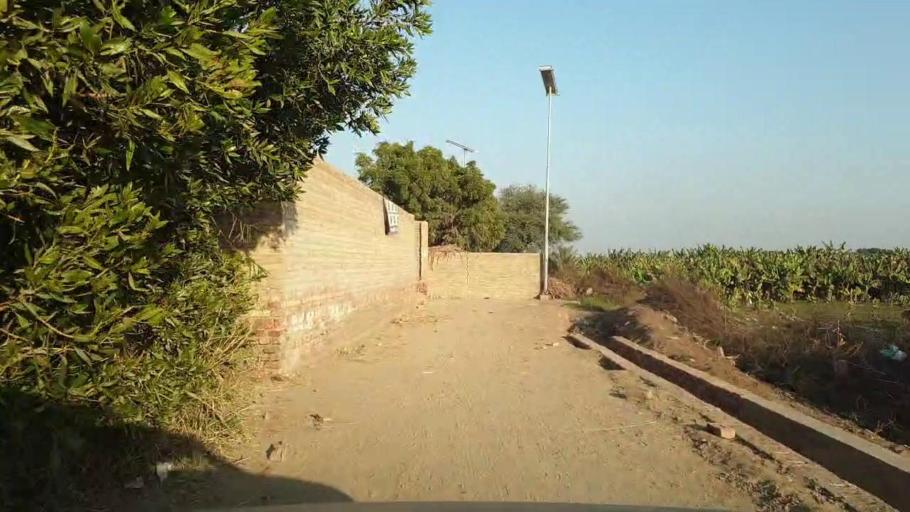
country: PK
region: Sindh
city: Tando Allahyar
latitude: 25.3358
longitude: 68.6855
